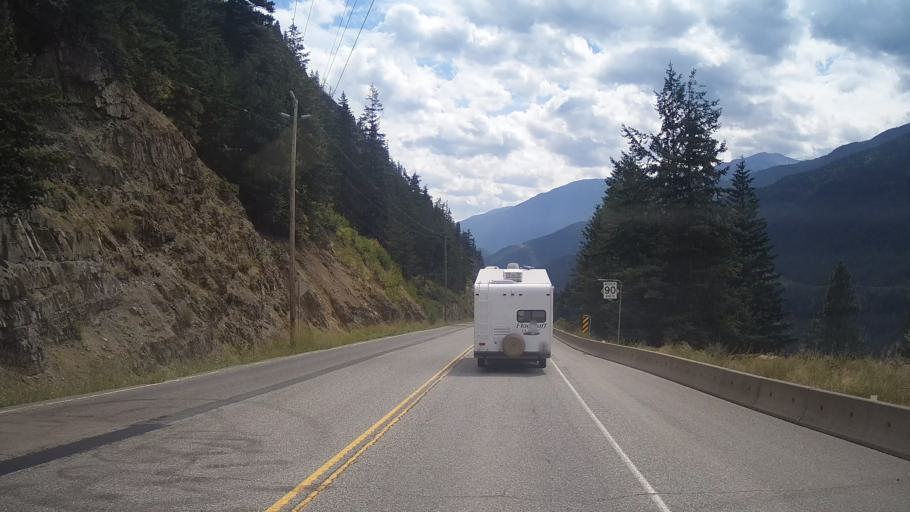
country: CA
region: British Columbia
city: Hope
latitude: 50.0744
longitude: -121.5469
